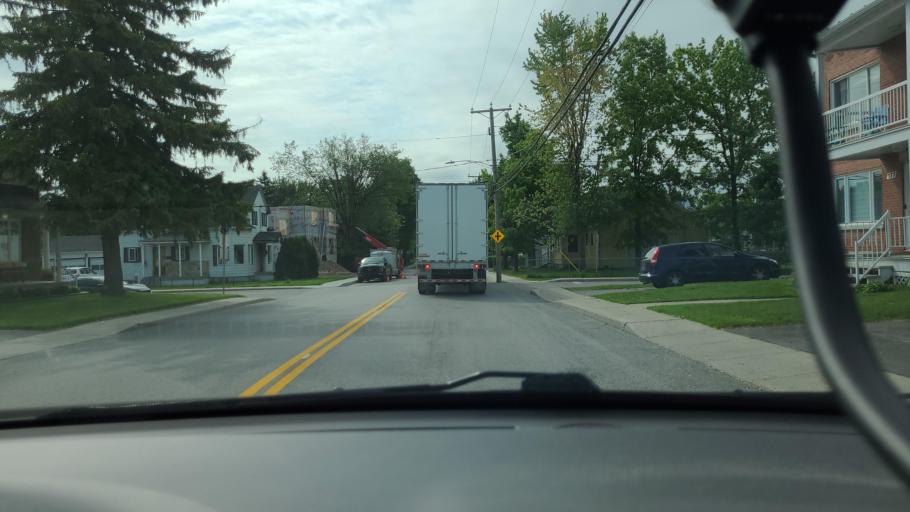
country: CA
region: Quebec
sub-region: Lanaudiere
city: Crabtree
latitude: 45.9651
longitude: -73.4752
